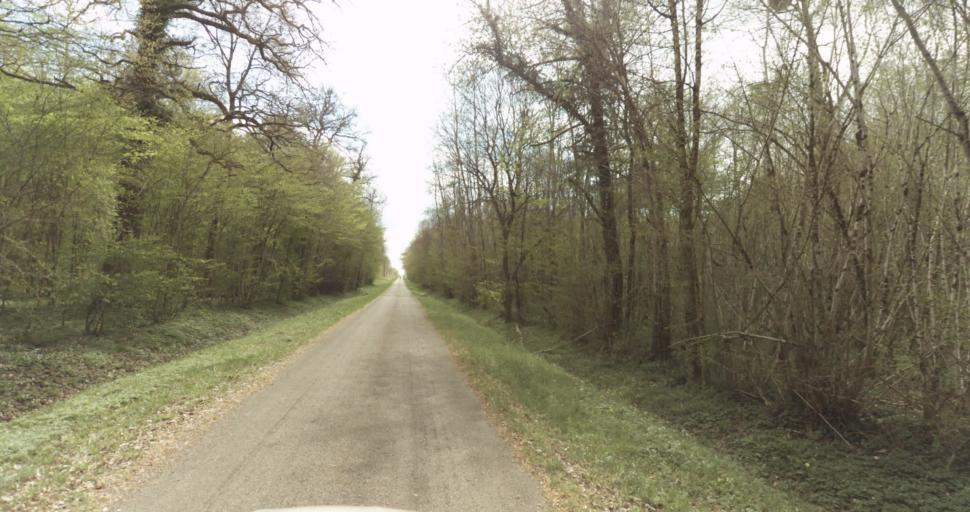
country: FR
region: Bourgogne
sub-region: Departement de la Cote-d'Or
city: Auxonne
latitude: 47.1864
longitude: 5.4501
